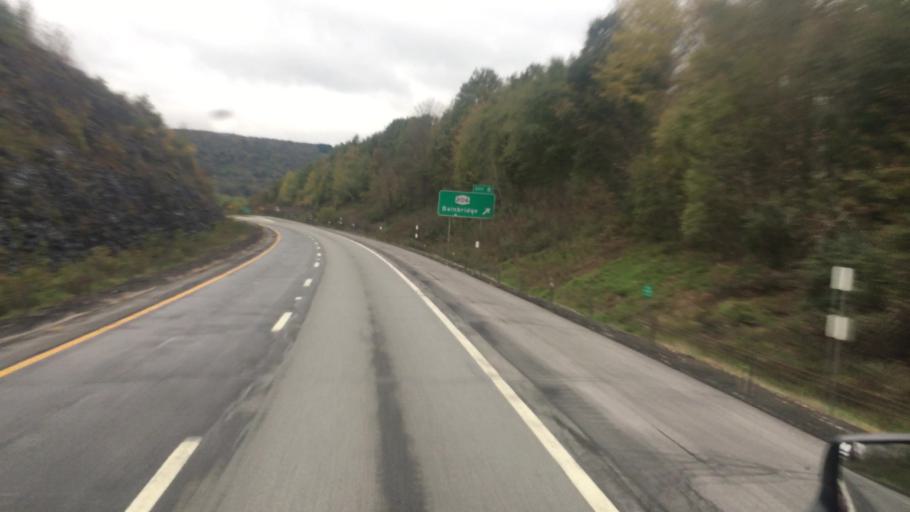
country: US
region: New York
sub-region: Chenango County
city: Bainbridge
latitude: 42.2944
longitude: -75.4643
